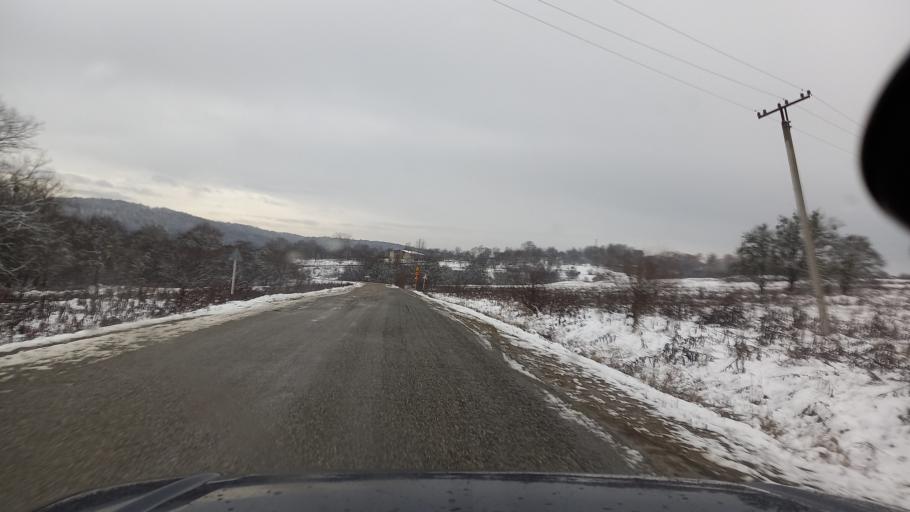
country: RU
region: Adygeya
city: Abadzekhskaya
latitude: 44.3592
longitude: 40.3995
